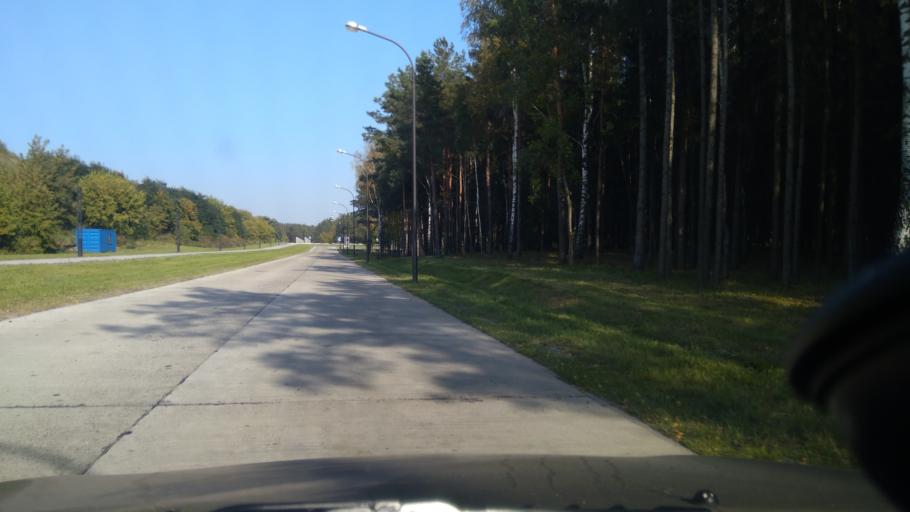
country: BY
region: Minsk
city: Vyaliki Trastsyanets
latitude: 53.8371
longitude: 27.7314
